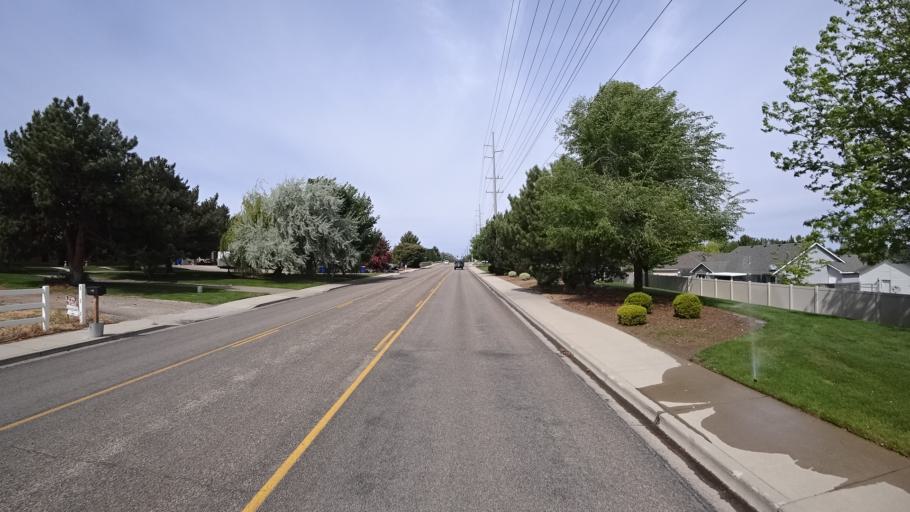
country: US
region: Idaho
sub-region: Ada County
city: Garden City
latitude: 43.5756
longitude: -116.3096
